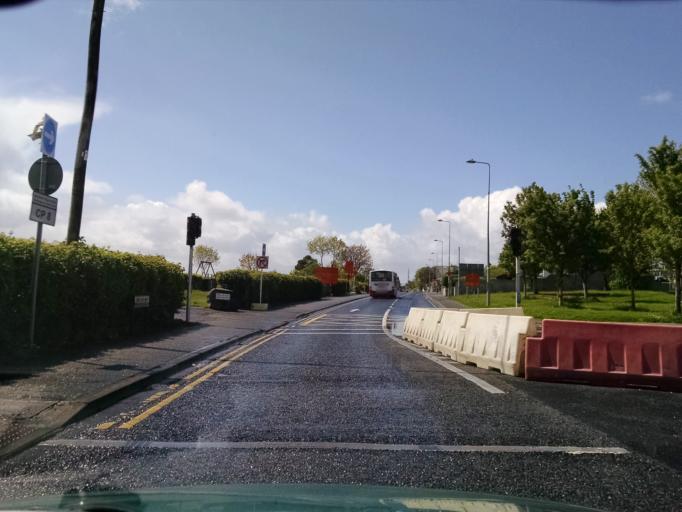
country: IE
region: Connaught
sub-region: County Galway
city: Gaillimh
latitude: 53.2804
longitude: -9.0353
